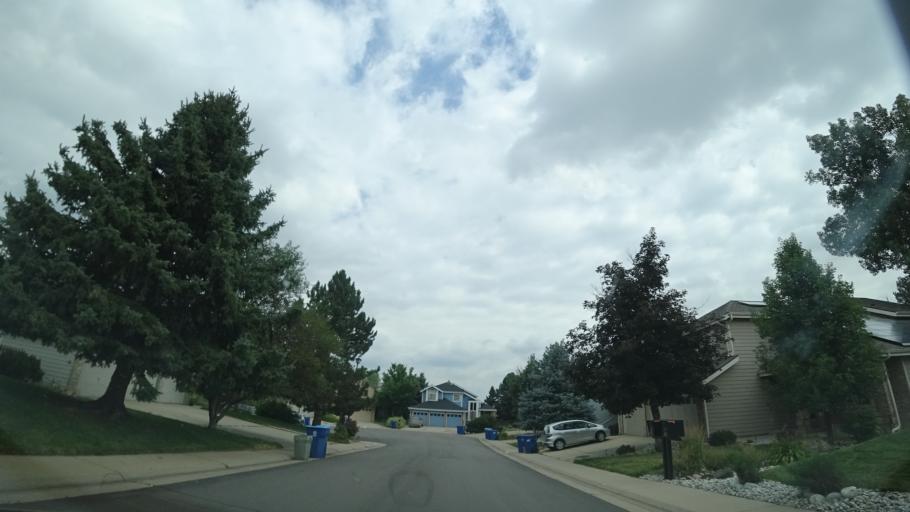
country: US
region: Colorado
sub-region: Jefferson County
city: West Pleasant View
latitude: 39.7176
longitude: -105.1669
